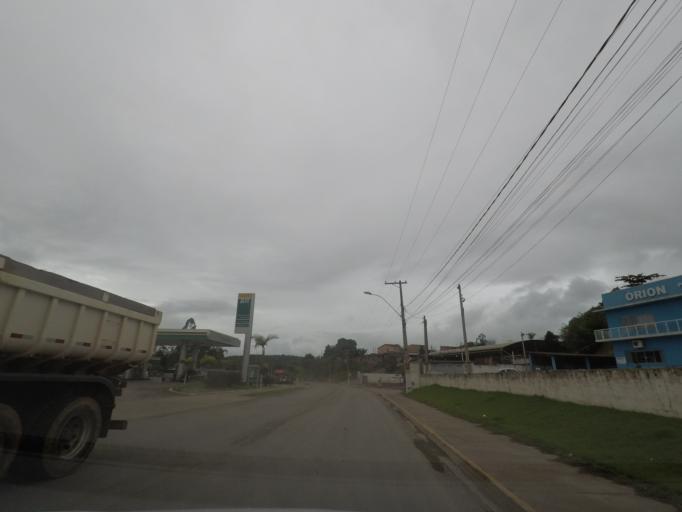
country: BR
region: Sao Paulo
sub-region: Cajati
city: Cajati
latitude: -24.7218
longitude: -48.0996
